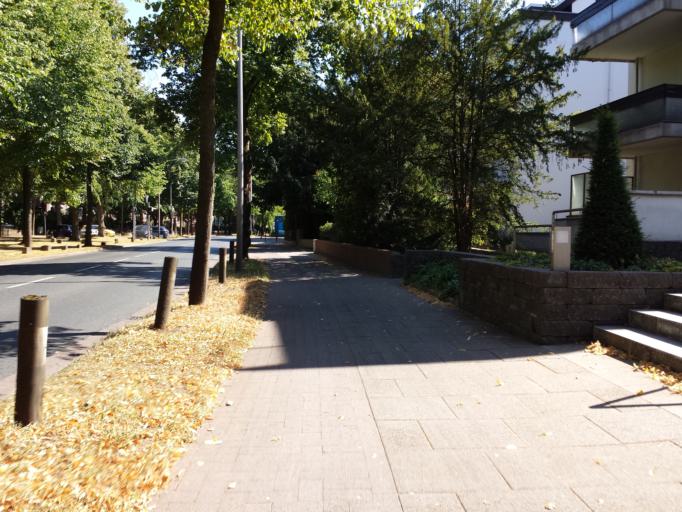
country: DE
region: Bremen
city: Bremen
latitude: 53.0791
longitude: 8.8548
